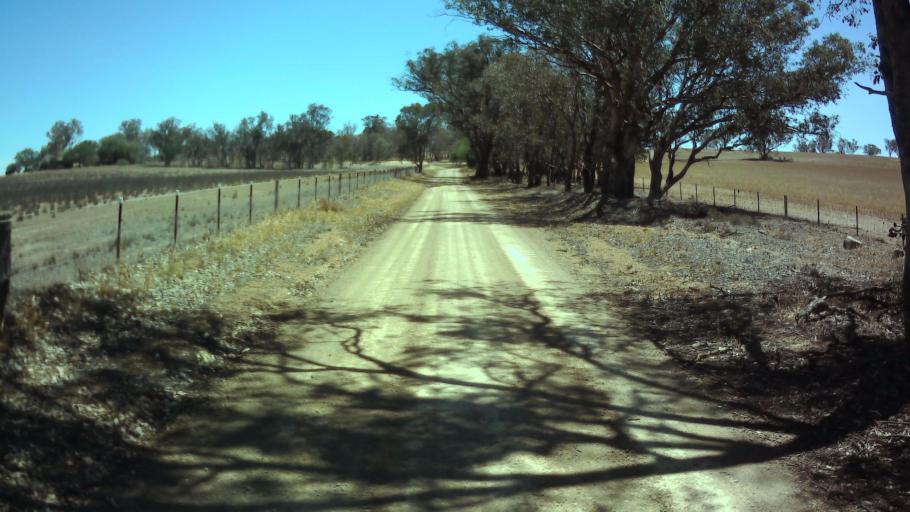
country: AU
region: New South Wales
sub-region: Weddin
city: Grenfell
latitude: -33.9300
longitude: 148.1564
